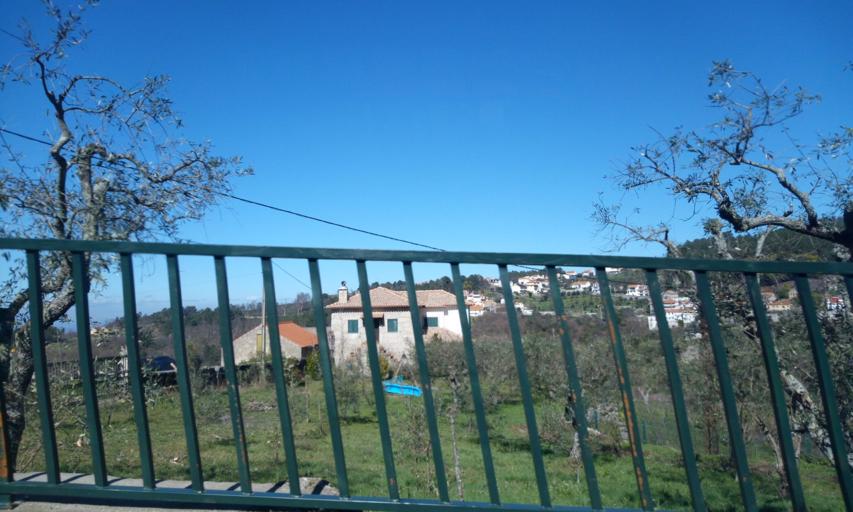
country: PT
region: Guarda
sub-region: Manteigas
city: Manteigas
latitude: 40.4671
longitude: -7.6009
